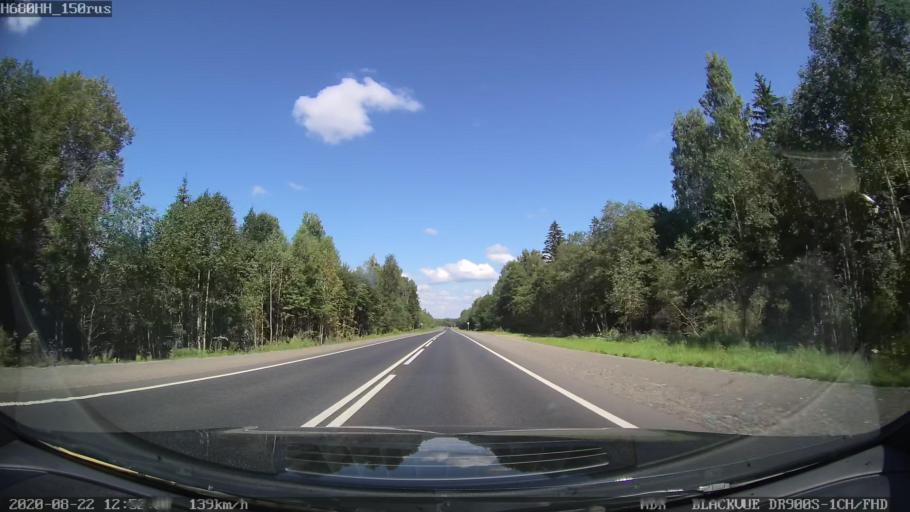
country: RU
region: Tverskaya
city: Rameshki
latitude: 57.4945
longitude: 36.2542
